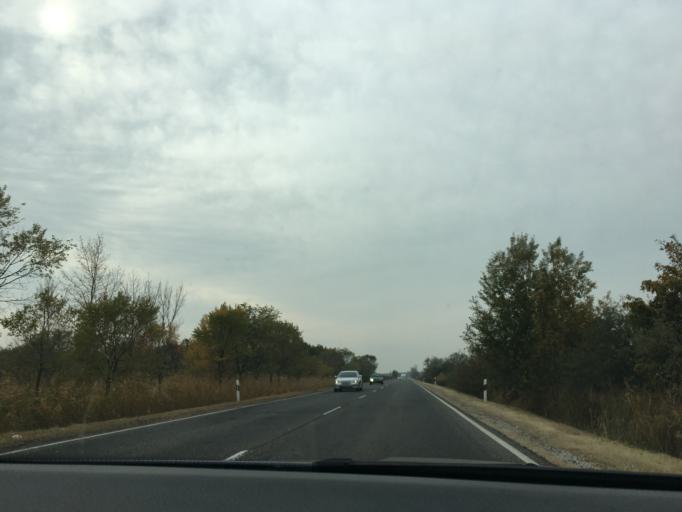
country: HU
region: Jasz-Nagykun-Szolnok
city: Karcag
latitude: 47.2685
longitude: 20.8634
